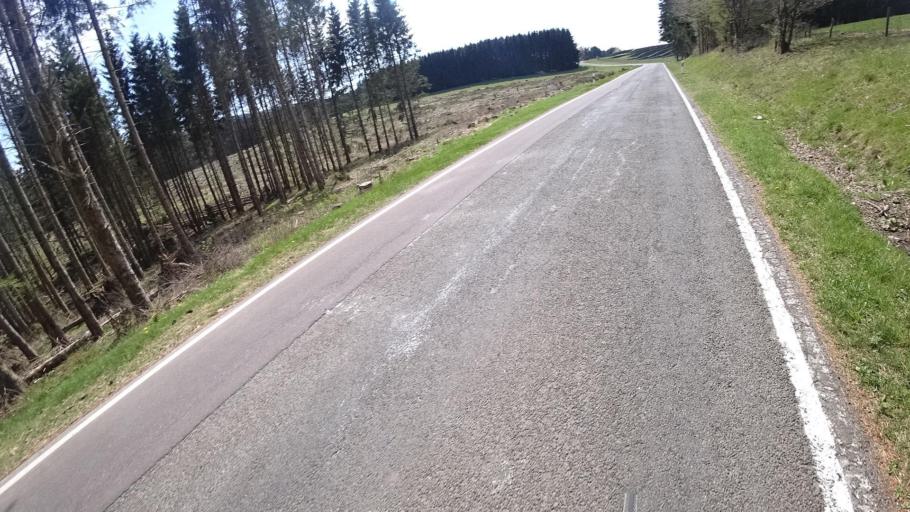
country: DE
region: Rheinland-Pfalz
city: Kell
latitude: 49.6349
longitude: 6.8481
